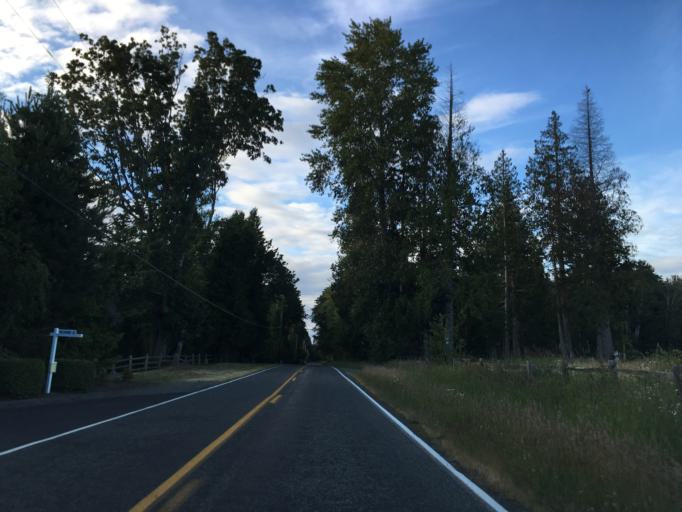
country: CA
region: British Columbia
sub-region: Greater Vancouver Regional District
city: White Rock
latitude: 48.9495
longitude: -122.8178
